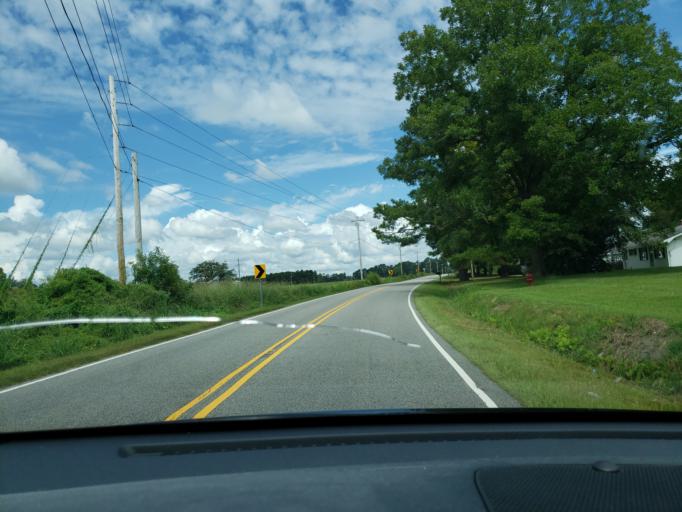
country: US
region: North Carolina
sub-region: Columbus County
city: Tabor City
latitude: 34.1788
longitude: -78.7875
